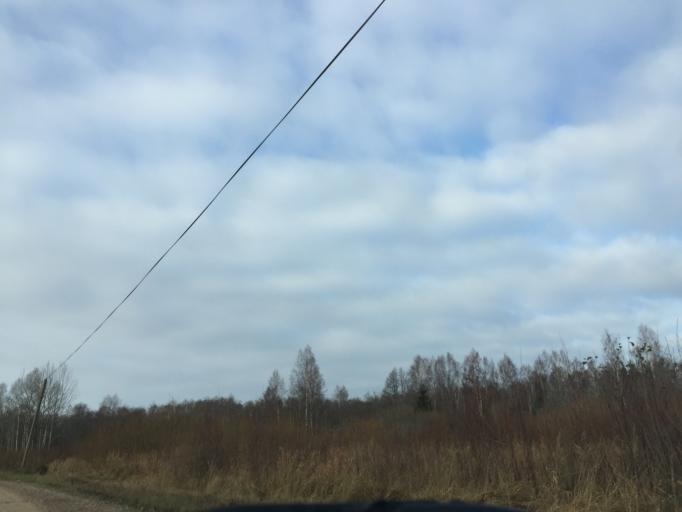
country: LV
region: Saulkrastu
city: Saulkrasti
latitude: 57.4668
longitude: 24.4044
